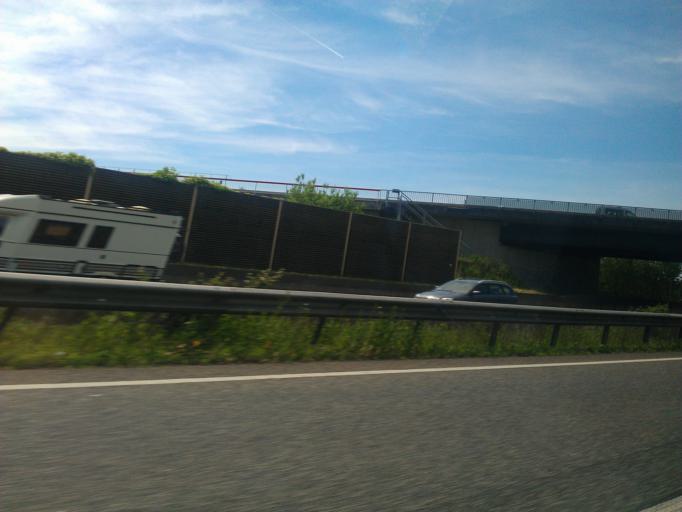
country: DE
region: Rheinland-Pfalz
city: Willroth
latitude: 50.5638
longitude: 7.5276
